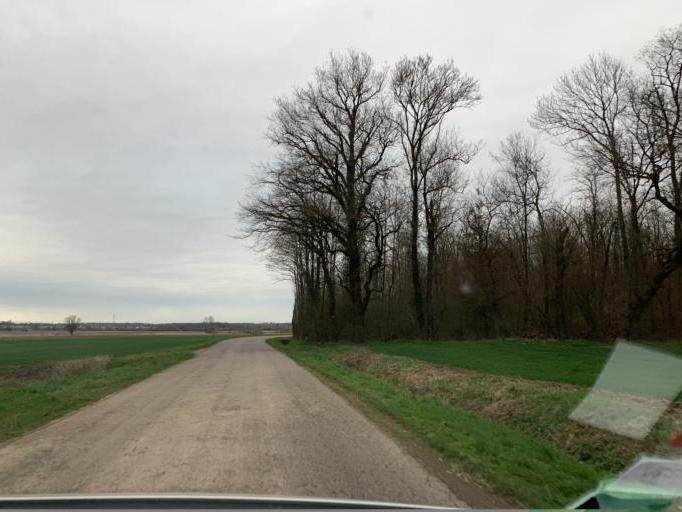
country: FR
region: Rhone-Alpes
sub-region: Departement de l'Ain
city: Mionnay
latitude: 45.8754
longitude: 4.9410
